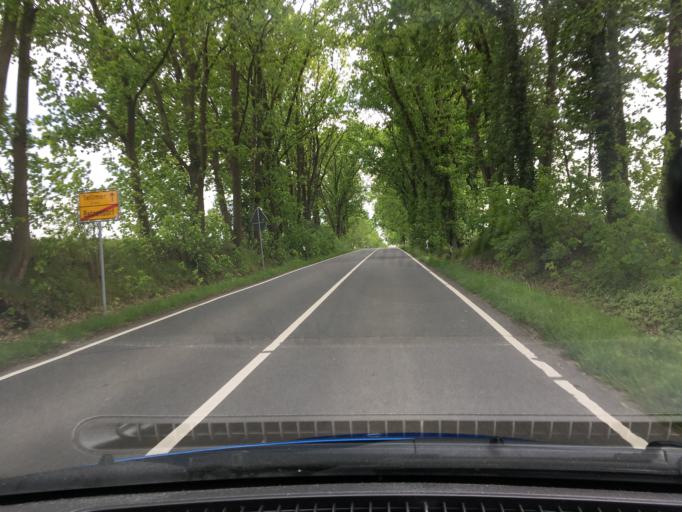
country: DE
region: Lower Saxony
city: Betzendorf
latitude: 53.1347
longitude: 10.3099
